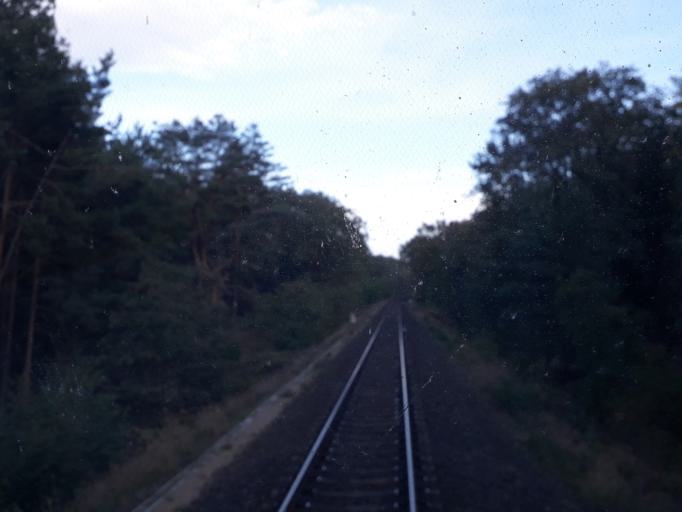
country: DE
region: Brandenburg
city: Perleberg
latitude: 53.0875
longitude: 11.9350
